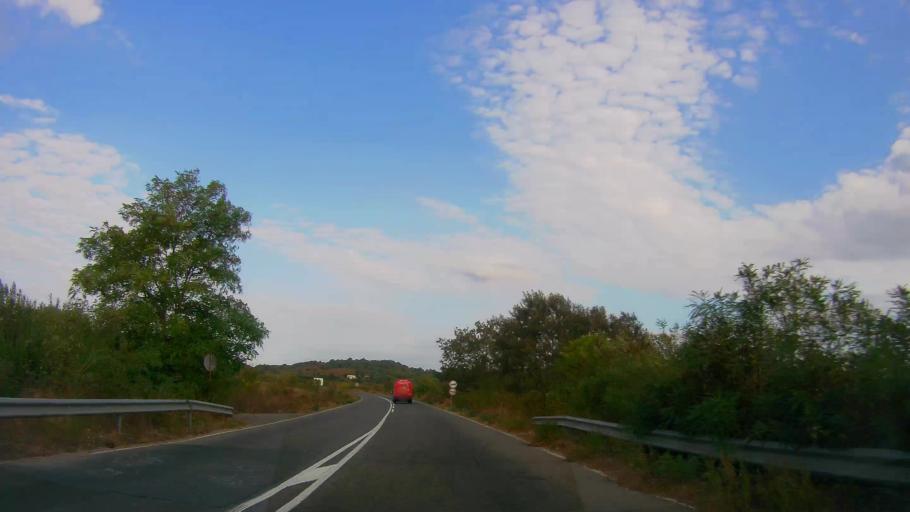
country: BG
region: Burgas
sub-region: Obshtina Sozopol
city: Sozopol
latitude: 42.3626
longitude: 27.6991
